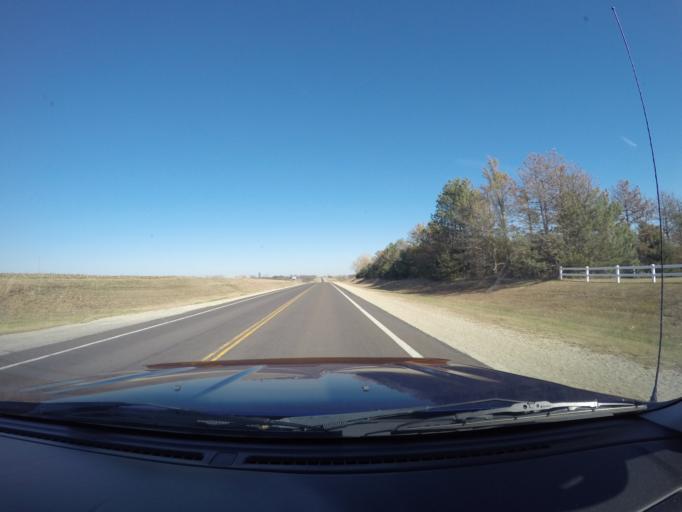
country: US
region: Kansas
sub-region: Marshall County
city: Blue Rapids
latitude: 39.6580
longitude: -96.7505
